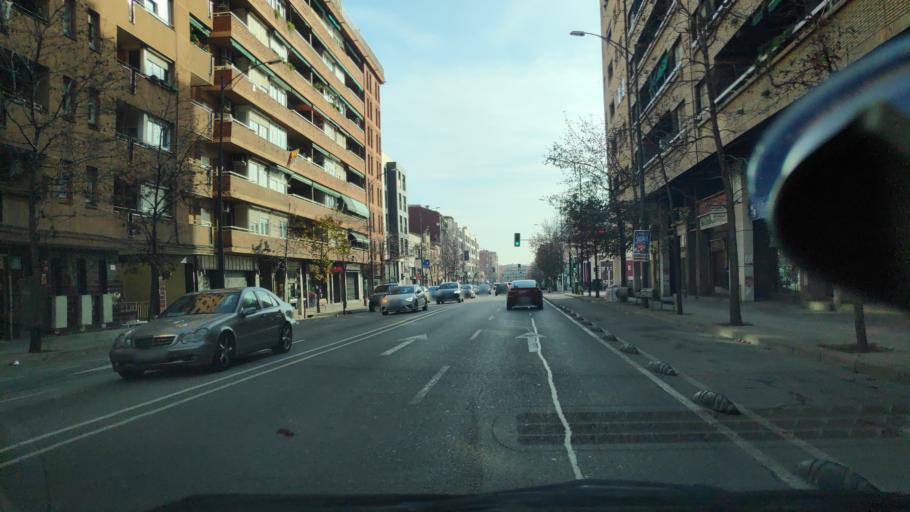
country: ES
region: Catalonia
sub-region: Provincia de Barcelona
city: Sabadell
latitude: 41.5491
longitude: 2.0985
